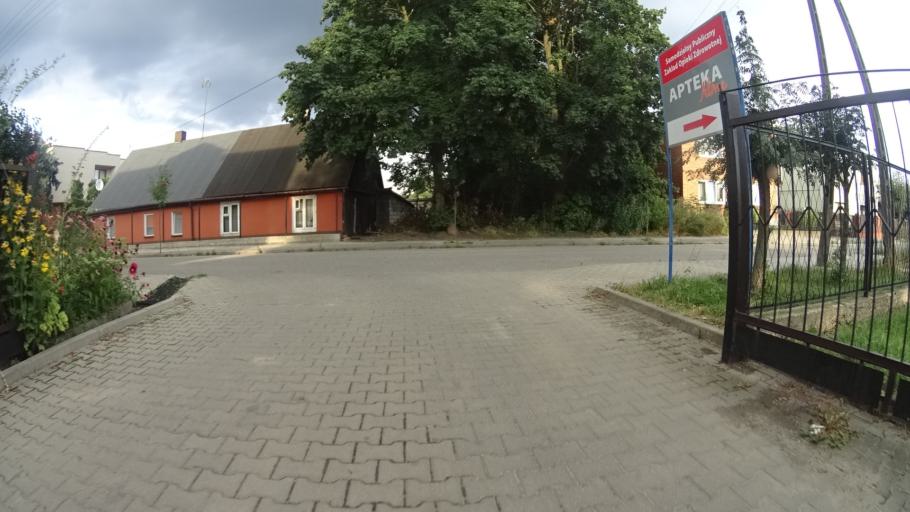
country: PL
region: Masovian Voivodeship
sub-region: Powiat grojecki
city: Mogielnica
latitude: 51.6906
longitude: 20.7257
